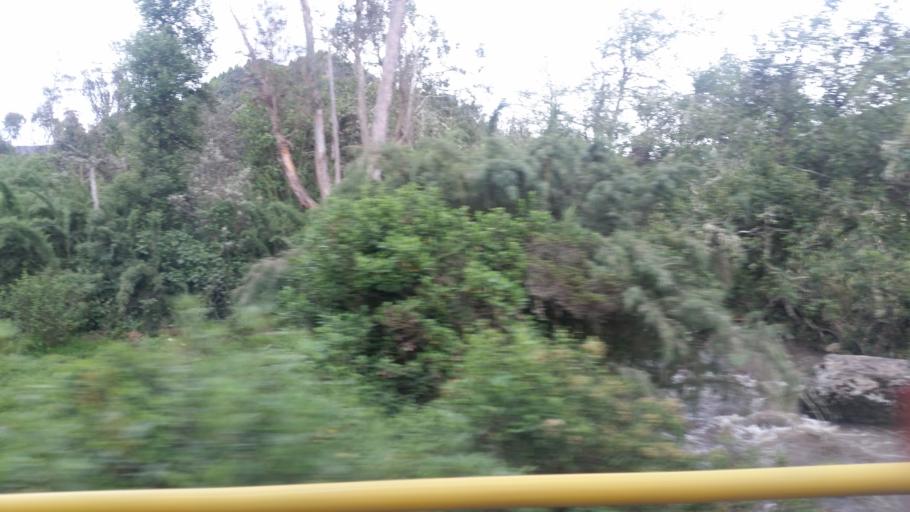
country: CO
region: Cundinamarca
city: Chipaque
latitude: 4.3858
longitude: -74.1381
